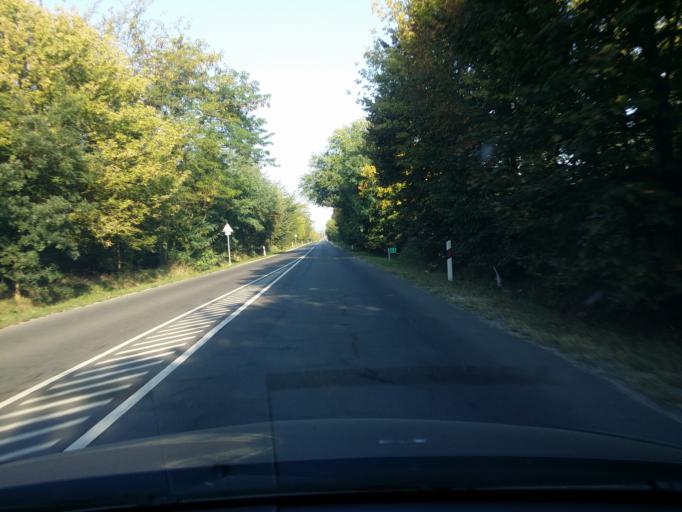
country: HU
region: Pest
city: Szod
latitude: 47.7482
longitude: 19.1723
